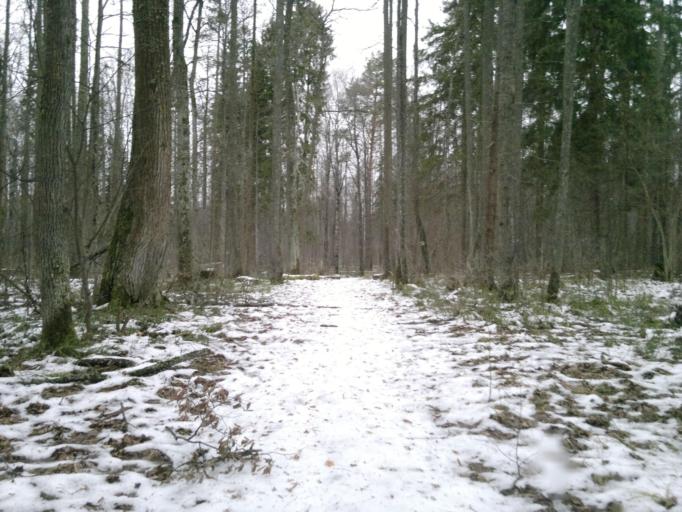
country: RU
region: Mariy-El
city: Yoshkar-Ola
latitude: 56.6126
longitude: 47.9469
